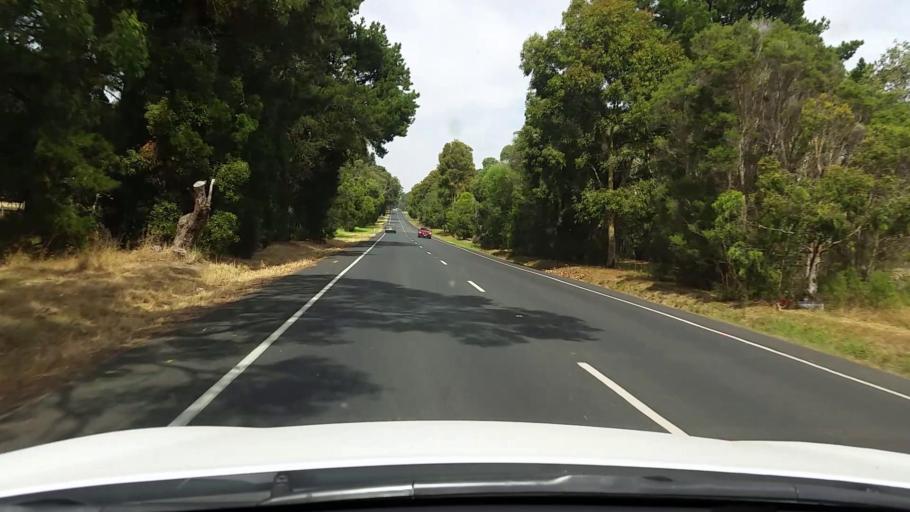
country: AU
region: Victoria
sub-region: Mornington Peninsula
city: Balnarring
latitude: -38.3643
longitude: 145.1403
